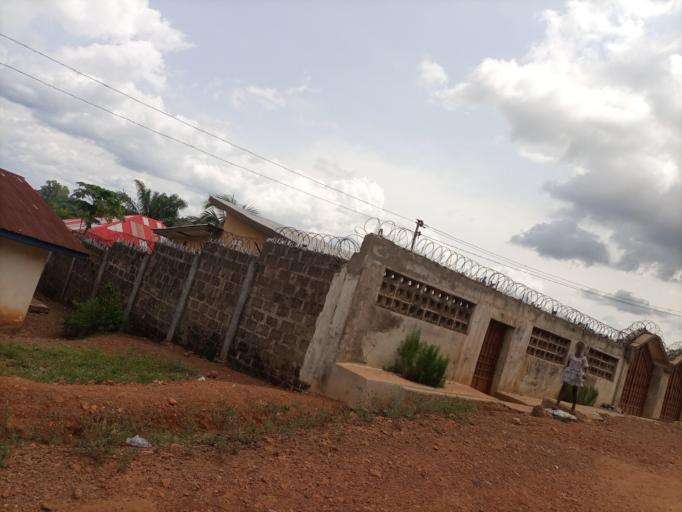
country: SL
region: Southern Province
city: Bo
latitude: 7.9499
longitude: -11.7394
